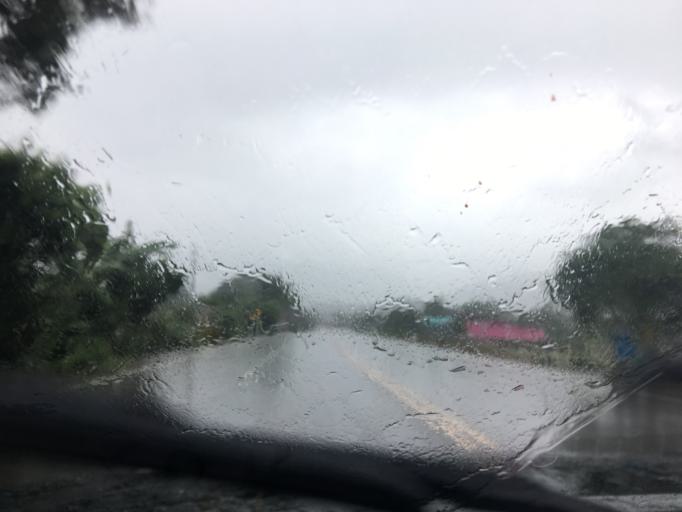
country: TH
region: Chiang Rai
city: Chiang Saen
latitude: 20.2993
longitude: 100.2295
